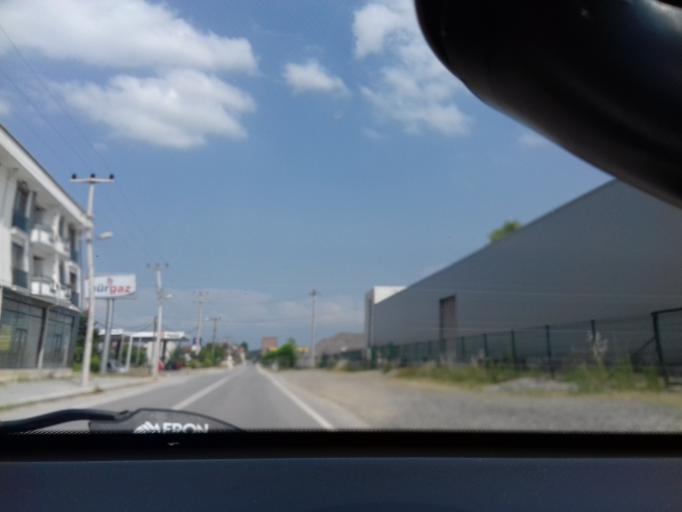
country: TR
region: Sakarya
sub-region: Merkez
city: Sapanca
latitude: 40.7136
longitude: 30.3491
